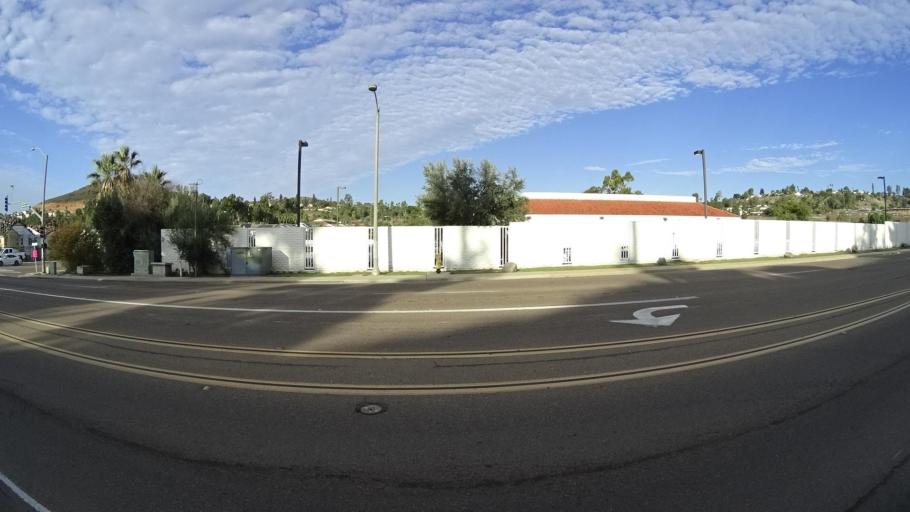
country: US
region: California
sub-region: San Diego County
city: Spring Valley
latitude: 32.7315
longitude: -116.9715
